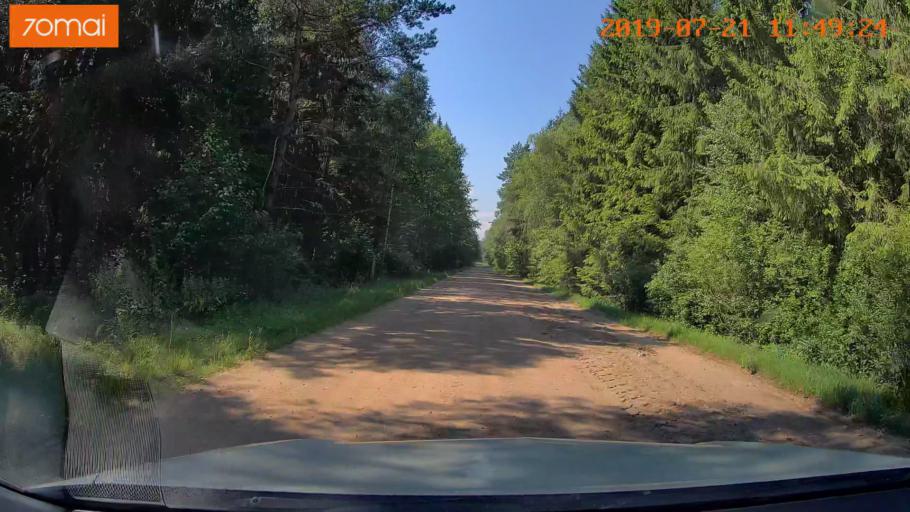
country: BY
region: Grodnenskaya
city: Lyubcha
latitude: 53.8926
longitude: 26.0394
